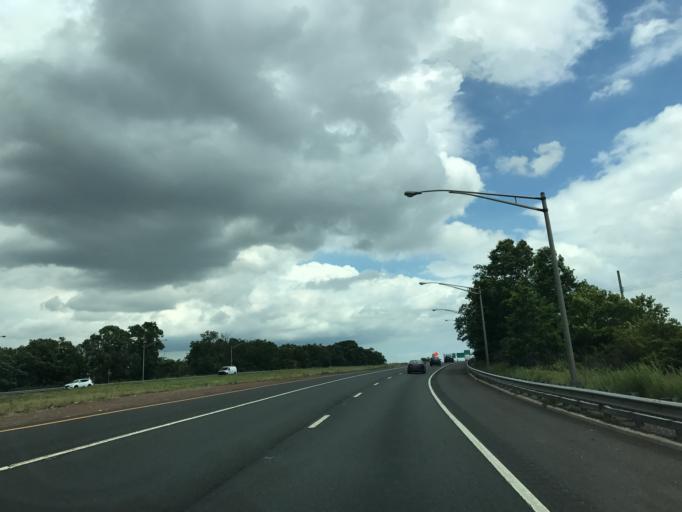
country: US
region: New Jersey
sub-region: Union County
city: Elizabeth
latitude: 40.6409
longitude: -74.2244
